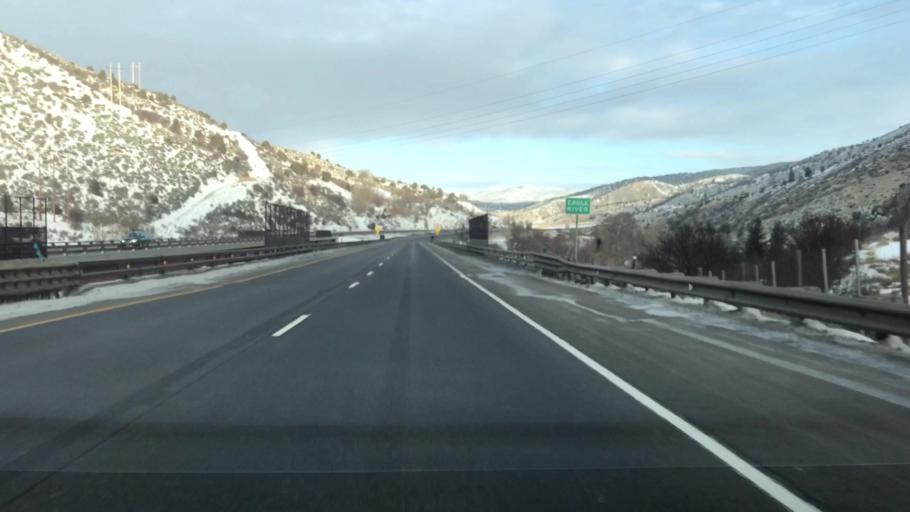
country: US
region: Colorado
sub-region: Eagle County
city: Edwards
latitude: 39.6729
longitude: -106.6461
